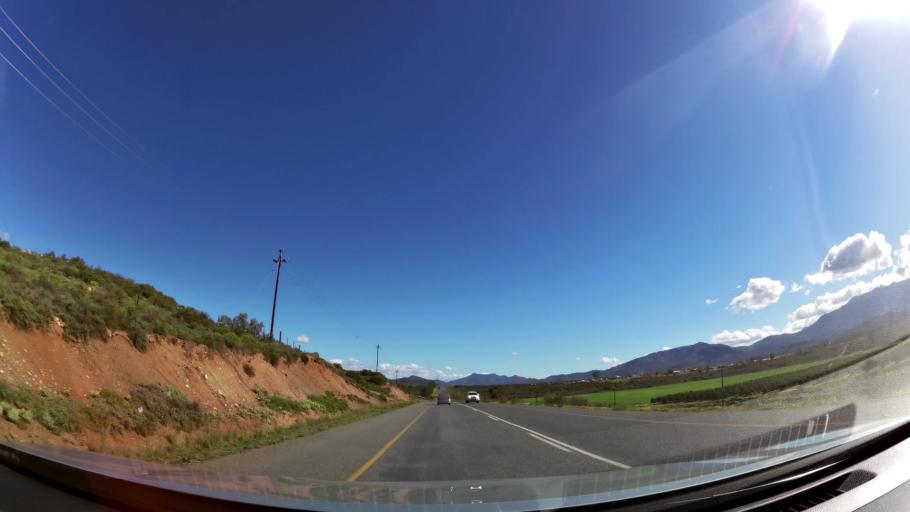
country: ZA
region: Western Cape
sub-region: Cape Winelands District Municipality
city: Ashton
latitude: -33.8143
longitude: 19.9330
